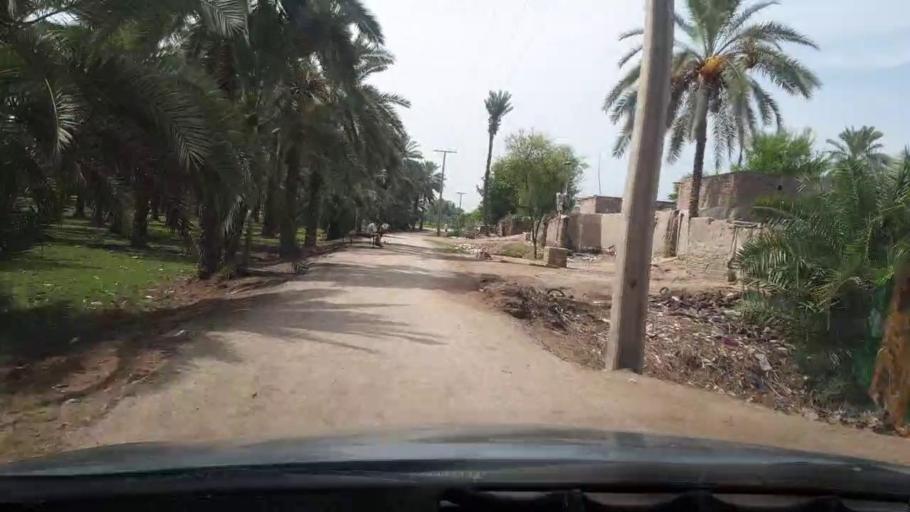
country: PK
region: Sindh
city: Khairpur
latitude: 27.4934
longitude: 68.7546
